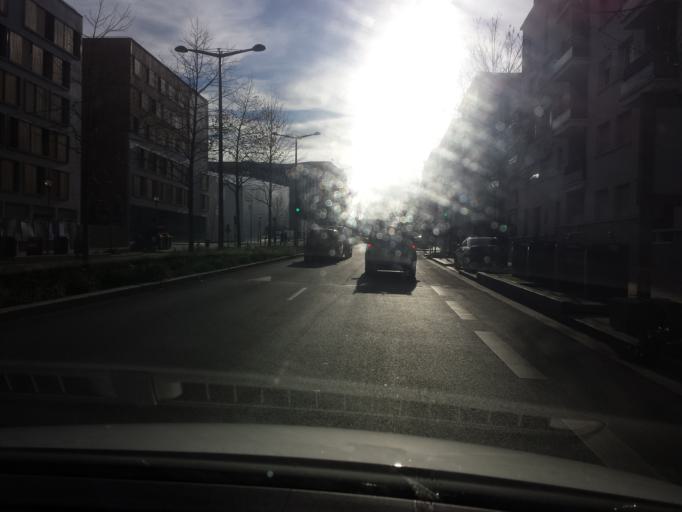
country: FR
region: Ile-de-France
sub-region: Departement de l'Essonne
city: Massy
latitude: 48.7288
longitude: 2.2700
